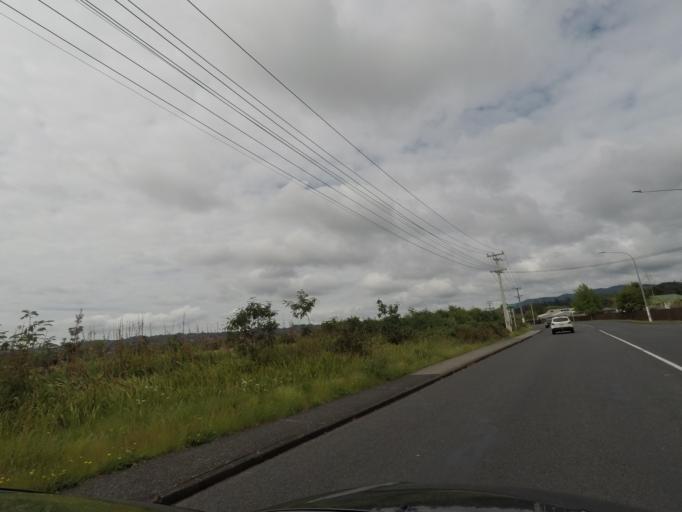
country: NZ
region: Auckland
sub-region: Auckland
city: Waitakere
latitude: -36.8999
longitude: 174.6230
